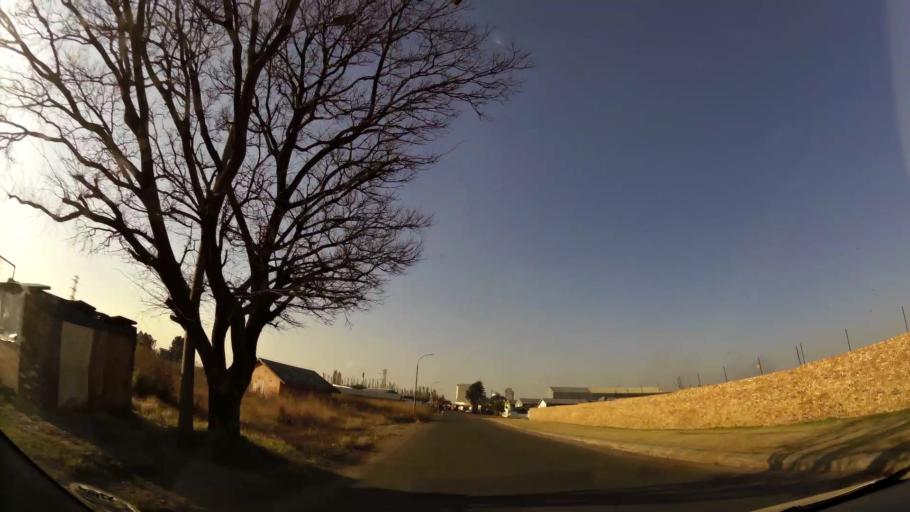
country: ZA
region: Gauteng
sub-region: West Rand District Municipality
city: Randfontein
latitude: -26.1945
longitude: 27.6855
